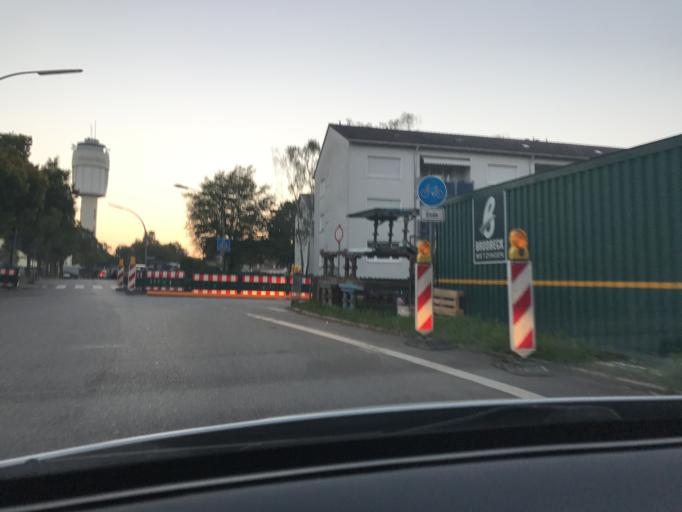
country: DE
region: Baden-Wuerttemberg
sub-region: Regierungsbezirk Stuttgart
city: Sindelfingen
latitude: 48.6998
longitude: 9.0137
